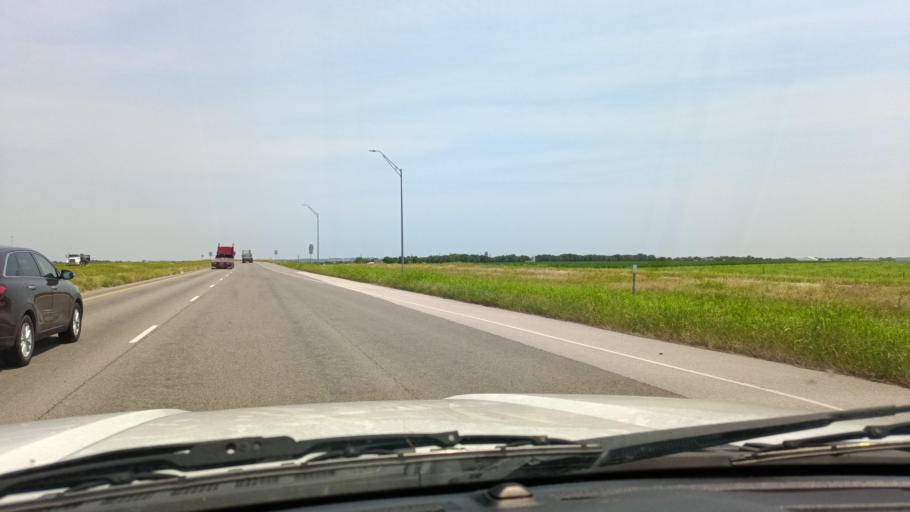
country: US
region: Texas
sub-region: Bell County
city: Little River-Academy
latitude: 31.0178
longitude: -97.3100
